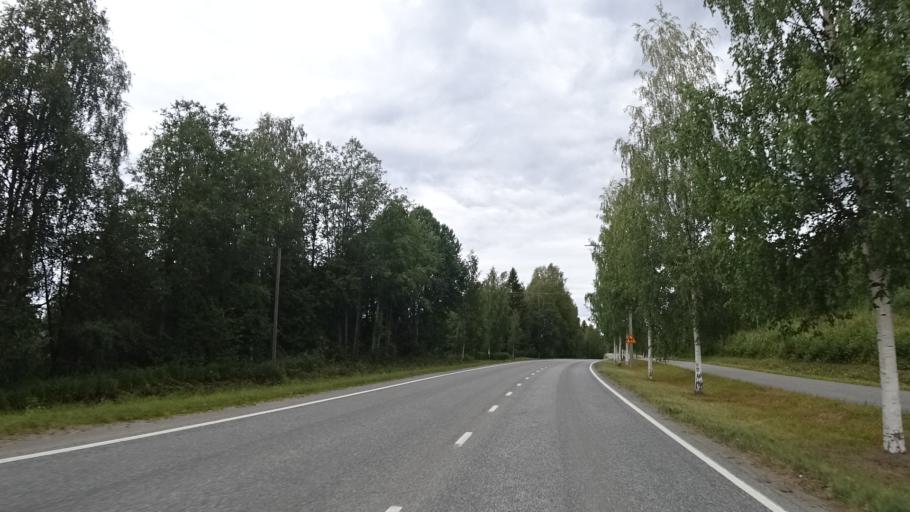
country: FI
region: North Karelia
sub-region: Joensuu
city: Ilomantsi
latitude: 62.6590
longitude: 30.9332
